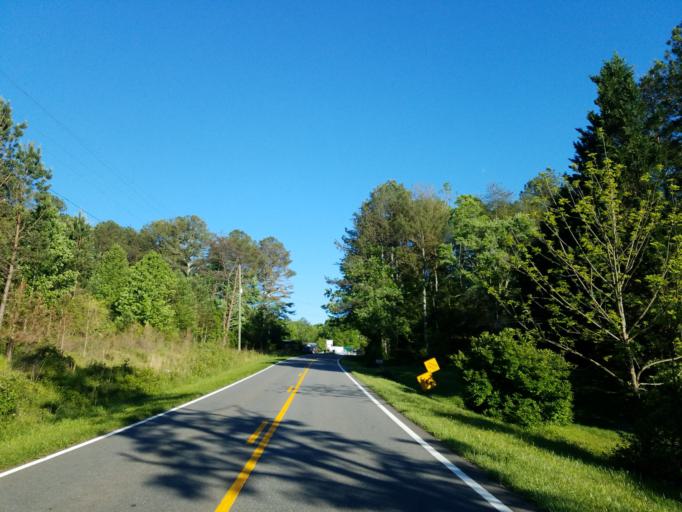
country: US
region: Georgia
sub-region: Gilmer County
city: Ellijay
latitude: 34.6757
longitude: -84.3704
